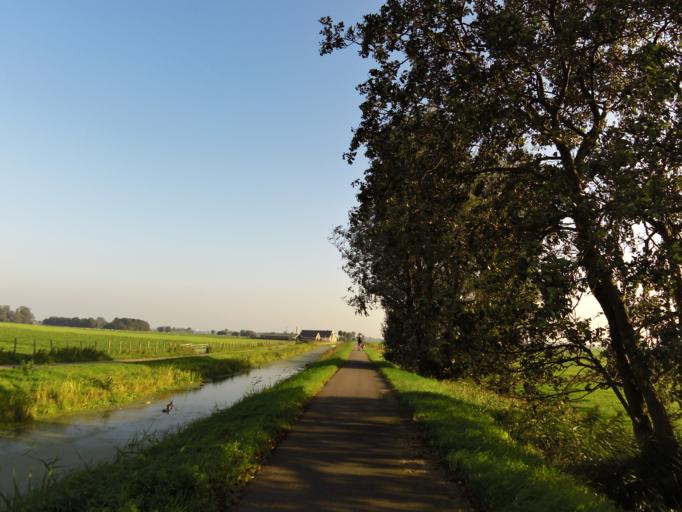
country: NL
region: South Holland
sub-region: Gemeente Leiderdorp
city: Leiderdorp
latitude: 52.1567
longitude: 4.5667
